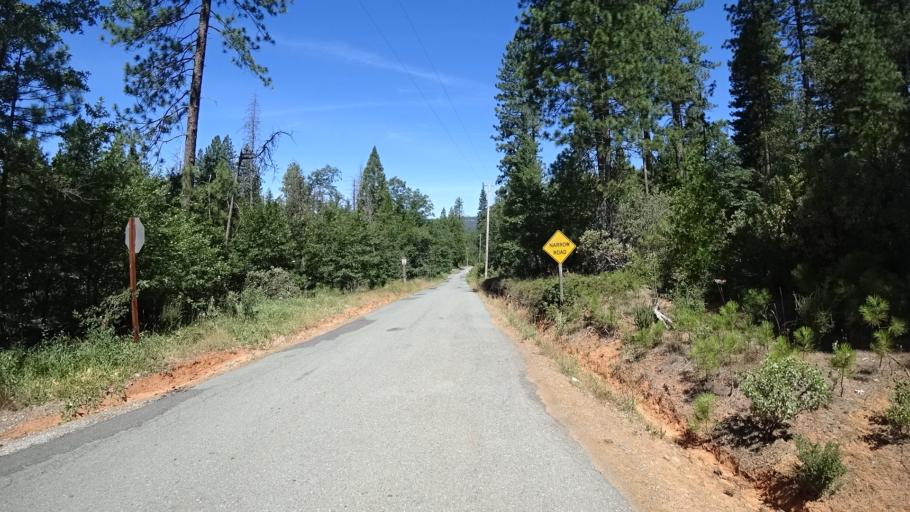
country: US
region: California
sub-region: Amador County
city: Pioneer
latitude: 38.4039
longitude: -120.5206
